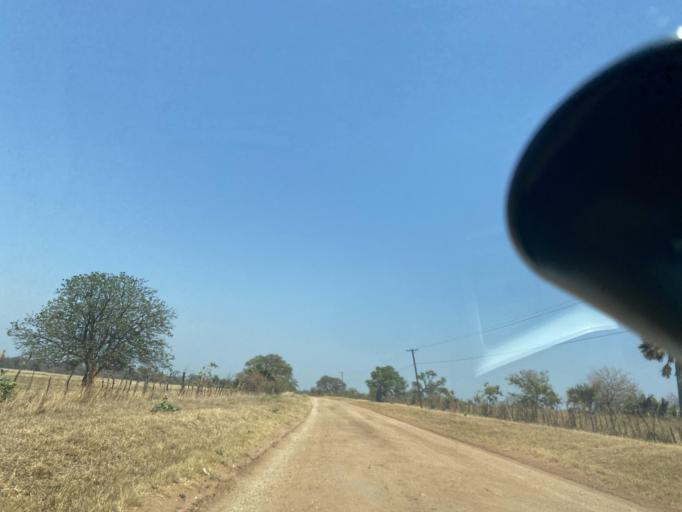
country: ZM
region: Lusaka
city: Lusaka
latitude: -15.5372
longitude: 28.0842
